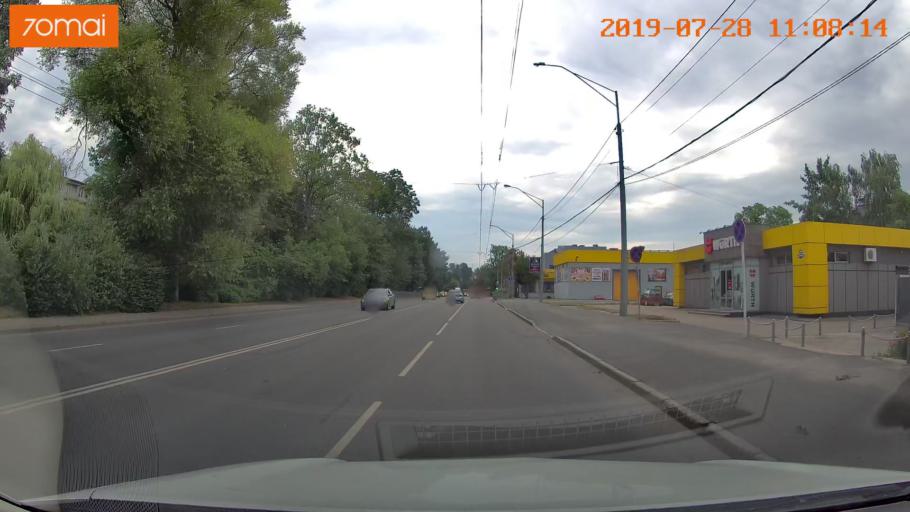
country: RU
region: Kaliningrad
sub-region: Gorod Kaliningrad
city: Kaliningrad
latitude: 54.7110
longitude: 20.4400
